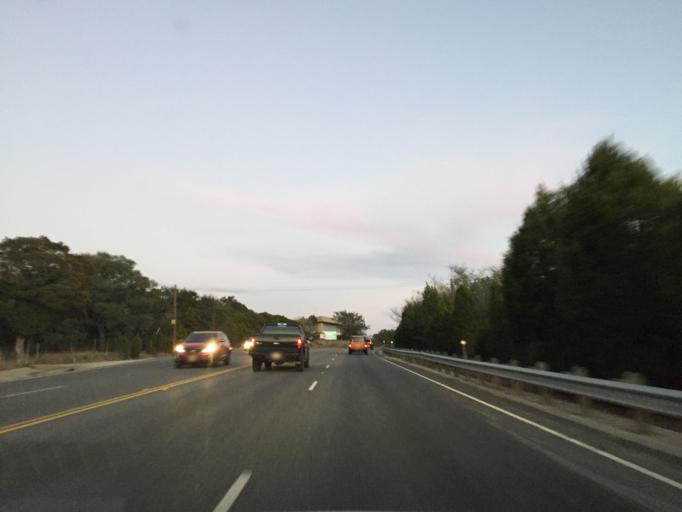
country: US
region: Texas
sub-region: Travis County
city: Jonestown
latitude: 30.5180
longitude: -97.8916
